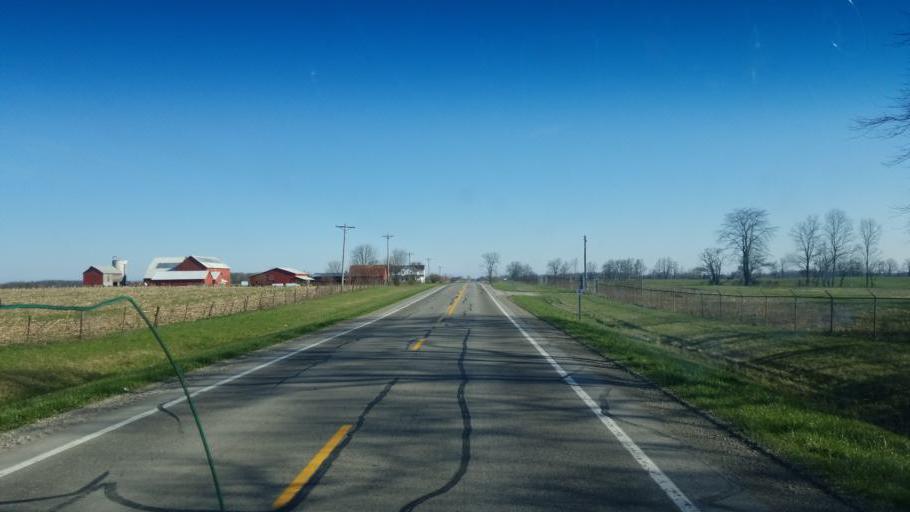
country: US
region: Ohio
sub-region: Hardin County
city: Kenton
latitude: 40.5686
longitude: -83.5896
